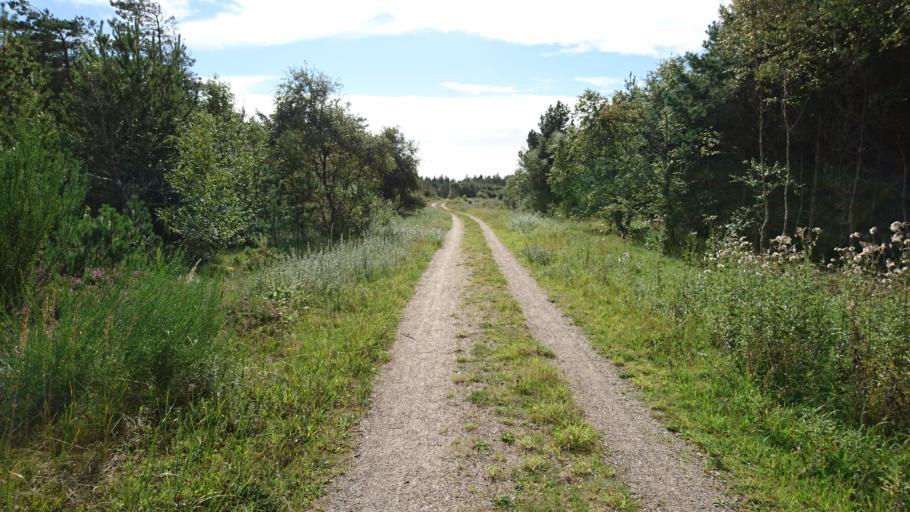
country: DK
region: North Denmark
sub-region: Frederikshavn Kommune
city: Skagen
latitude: 57.7144
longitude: 10.5143
